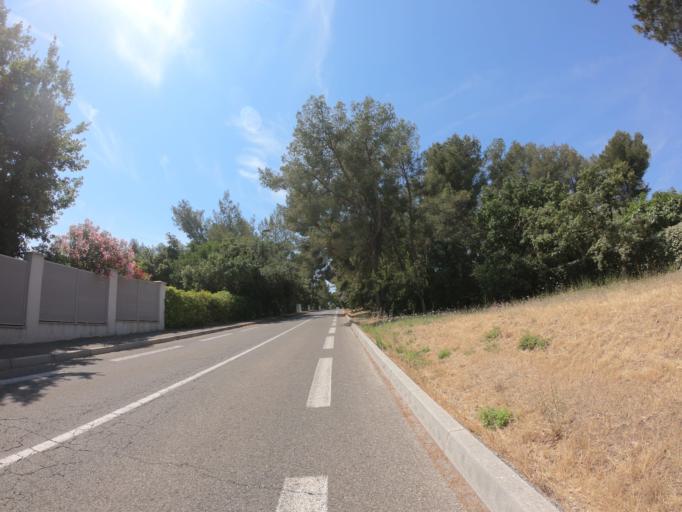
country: FR
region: Provence-Alpes-Cote d'Azur
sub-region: Departement du Var
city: La Garde
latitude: 43.1190
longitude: 5.9991
